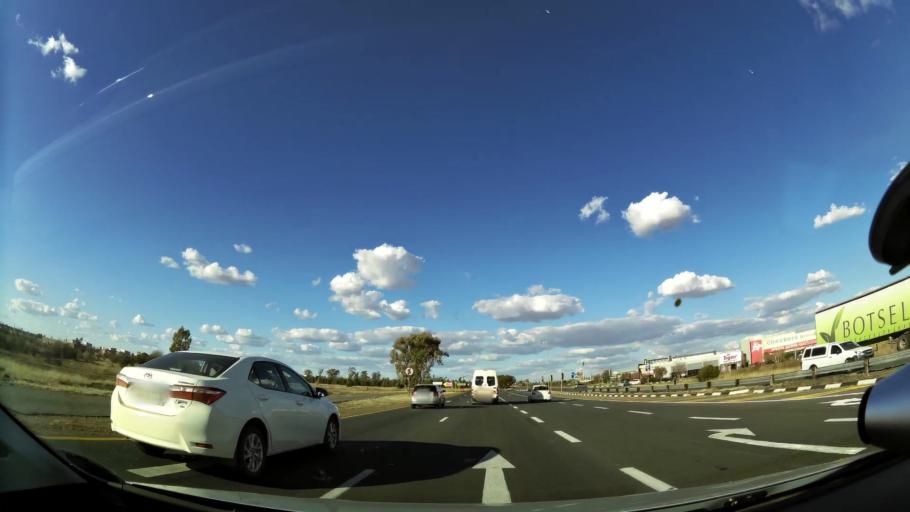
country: ZA
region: North-West
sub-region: Dr Kenneth Kaunda District Municipality
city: Klerksdorp
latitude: -26.8488
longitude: 26.6984
